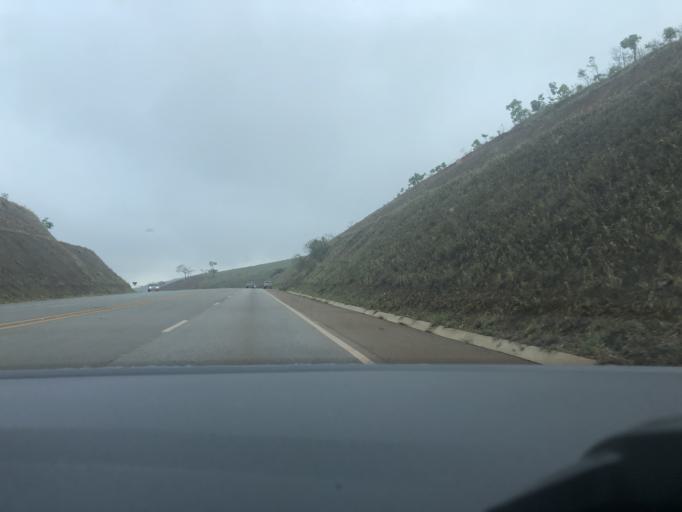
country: BR
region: Minas Gerais
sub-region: Congonhas
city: Congonhas
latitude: -20.6057
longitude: -43.9318
